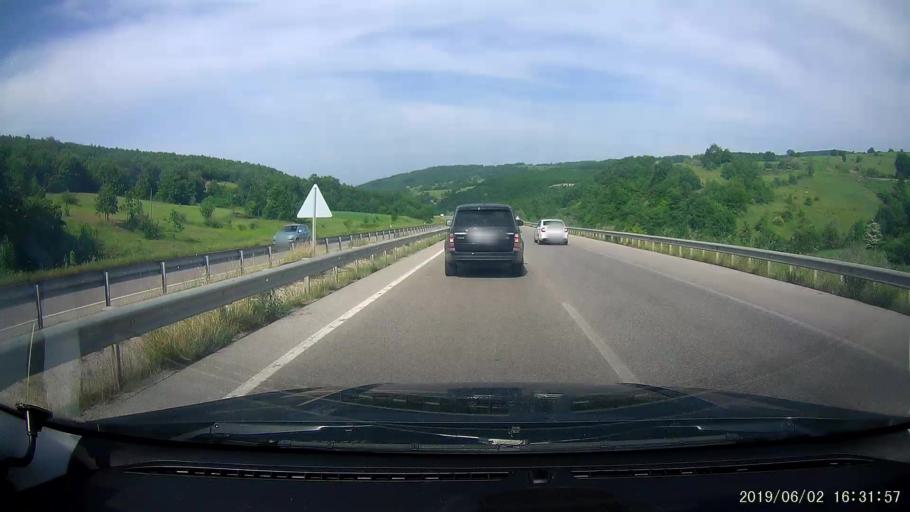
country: TR
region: Samsun
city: Ladik
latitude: 41.0362
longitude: 35.9095
